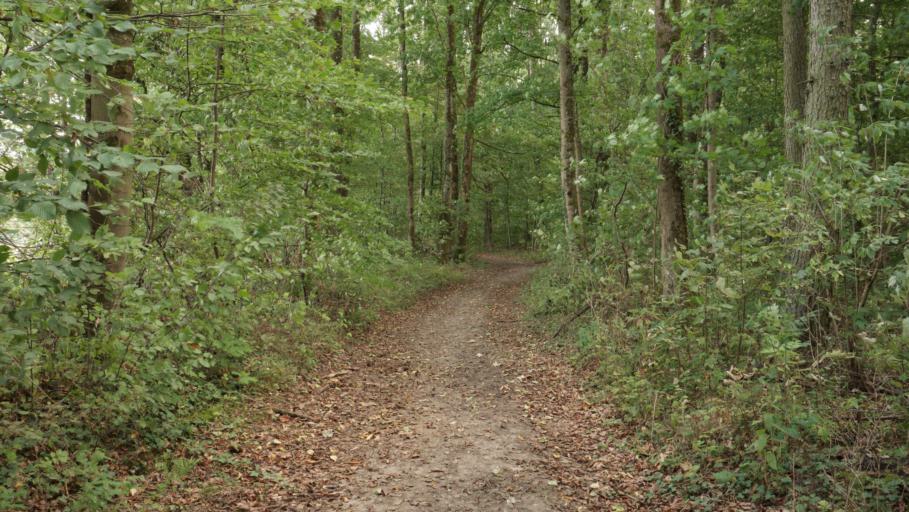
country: DE
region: Baden-Wuerttemberg
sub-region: Karlsruhe Region
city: Mosbach
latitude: 49.3534
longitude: 9.1674
